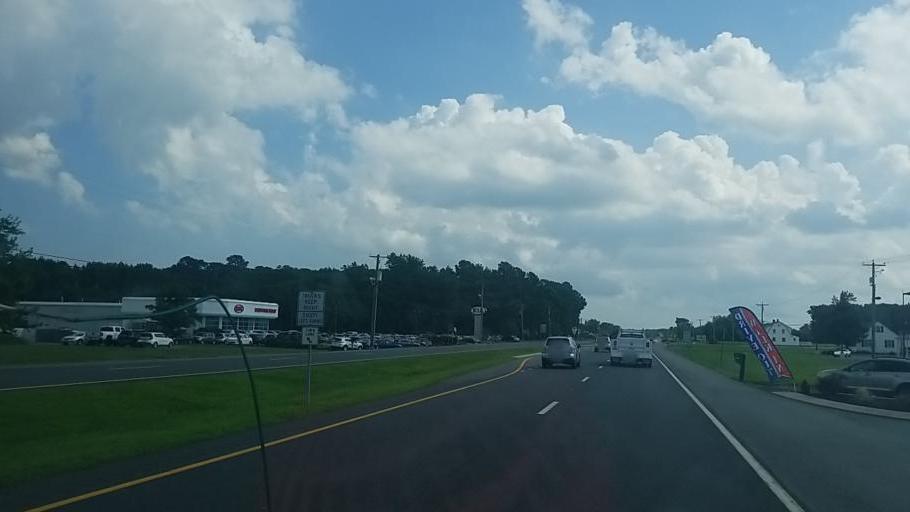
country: US
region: Delaware
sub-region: Sussex County
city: Selbyville
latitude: 38.4674
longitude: -75.2344
